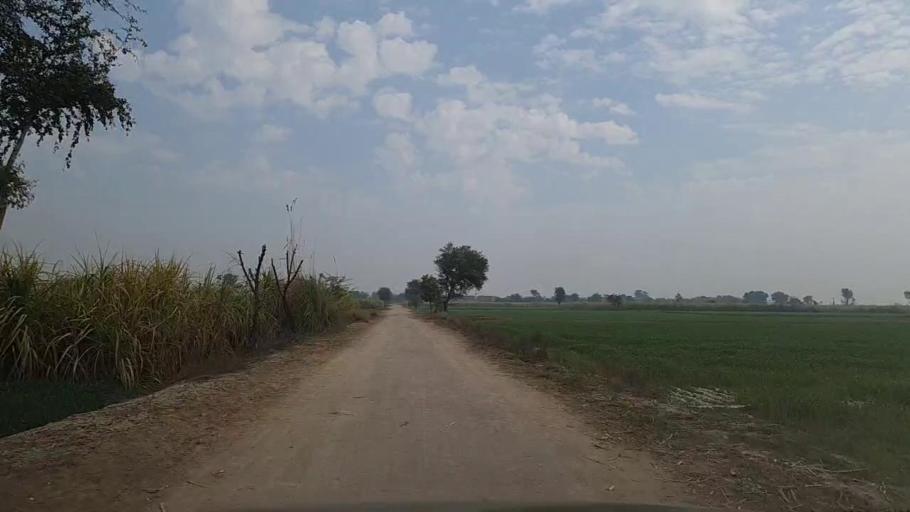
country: PK
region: Sindh
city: Daur
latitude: 26.3915
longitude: 68.3548
